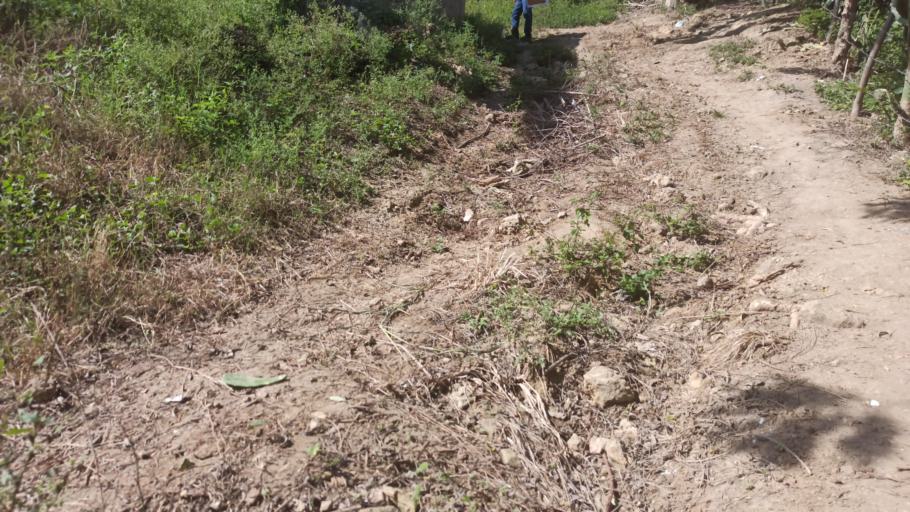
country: MX
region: Veracruz
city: Cazones de Herrera
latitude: 20.6410
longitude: -97.3099
